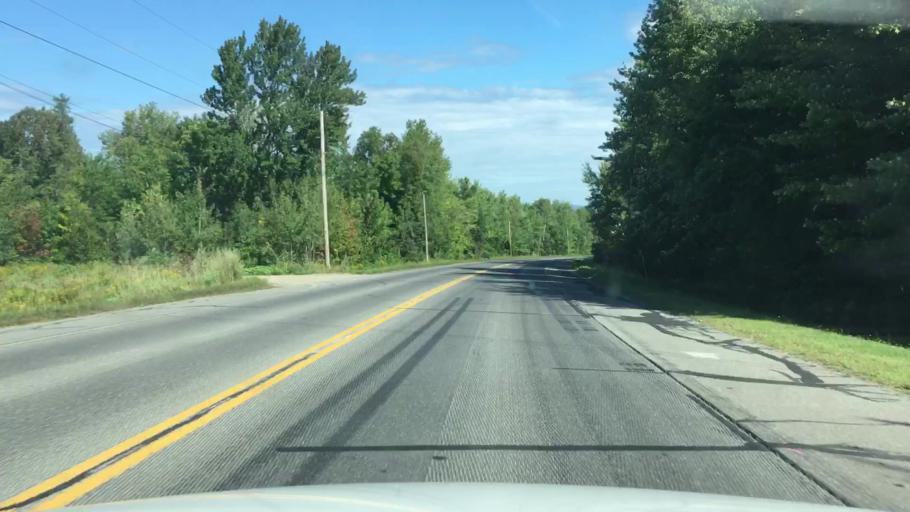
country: US
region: Maine
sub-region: Penobscot County
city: Newport
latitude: 44.8785
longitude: -69.2817
